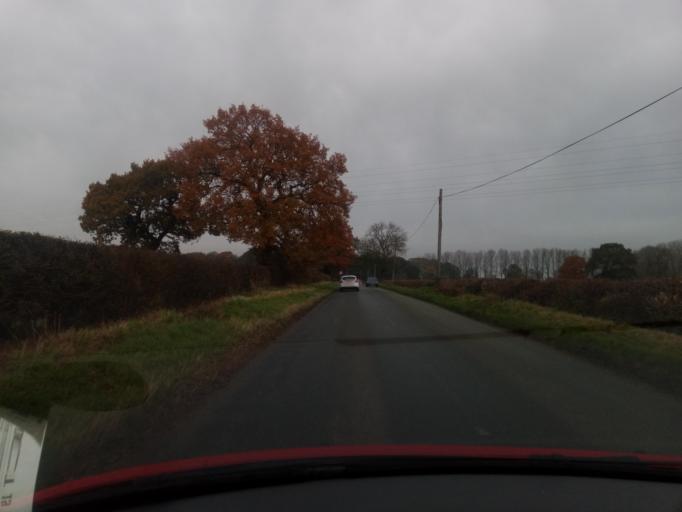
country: GB
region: England
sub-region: Derbyshire
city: Borrowash
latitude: 52.9331
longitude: -1.4035
